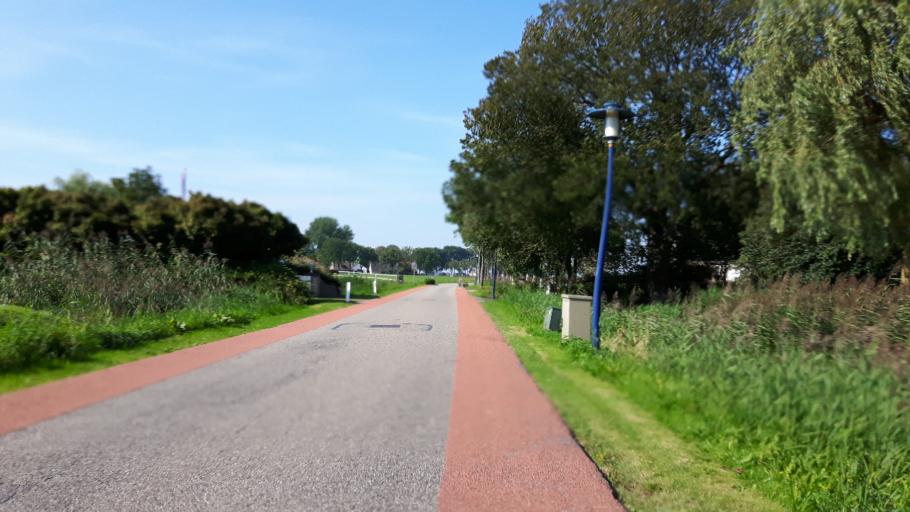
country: NL
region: Friesland
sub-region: Gemeente Ferwerderadiel
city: Ferwert
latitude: 53.3518
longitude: 5.8582
